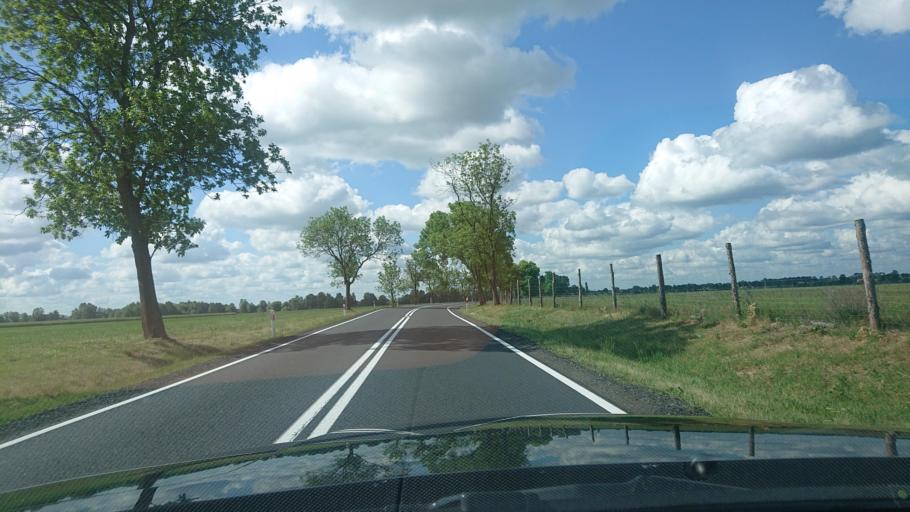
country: PL
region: Lower Silesian Voivodeship
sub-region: Powiat polkowicki
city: Radwanice
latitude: 51.5562
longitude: 15.9338
